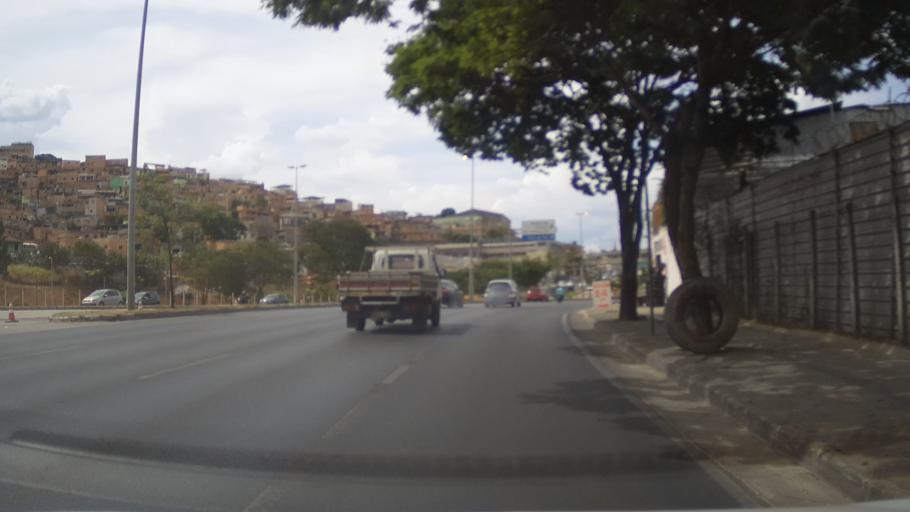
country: BR
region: Minas Gerais
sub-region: Belo Horizonte
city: Belo Horizonte
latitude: -19.8865
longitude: -43.9512
